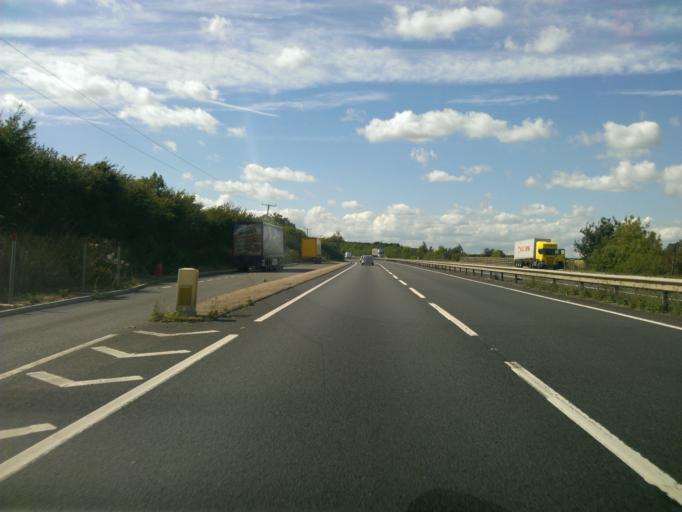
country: GB
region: England
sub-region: Northamptonshire
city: Thrapston
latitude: 52.3786
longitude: -0.4746
